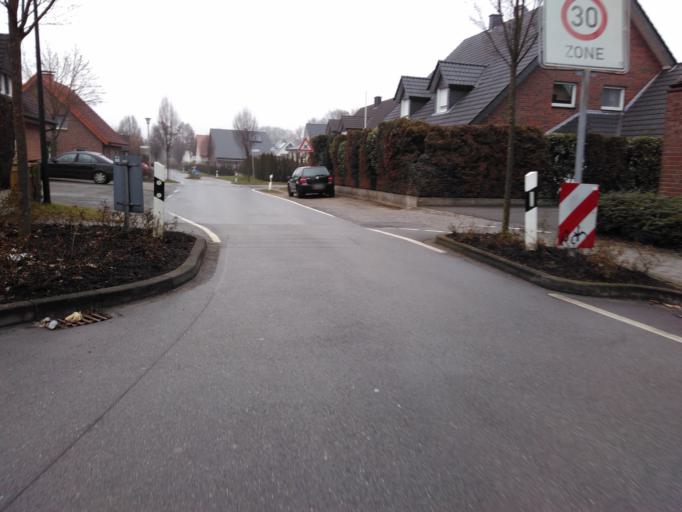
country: DE
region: North Rhine-Westphalia
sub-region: Regierungsbezirk Detmold
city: Verl
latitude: 51.8800
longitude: 8.4907
